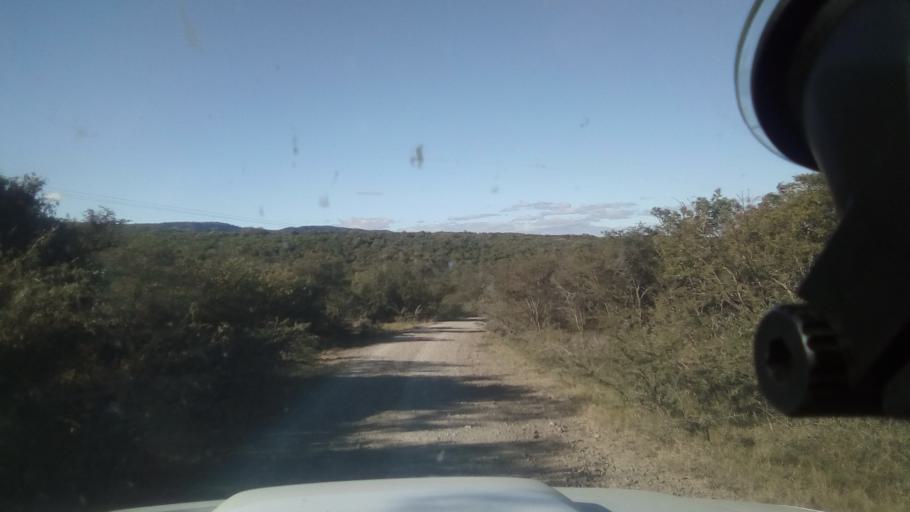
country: ZA
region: Eastern Cape
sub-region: Buffalo City Metropolitan Municipality
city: Bhisho
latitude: -32.7532
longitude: 27.3389
